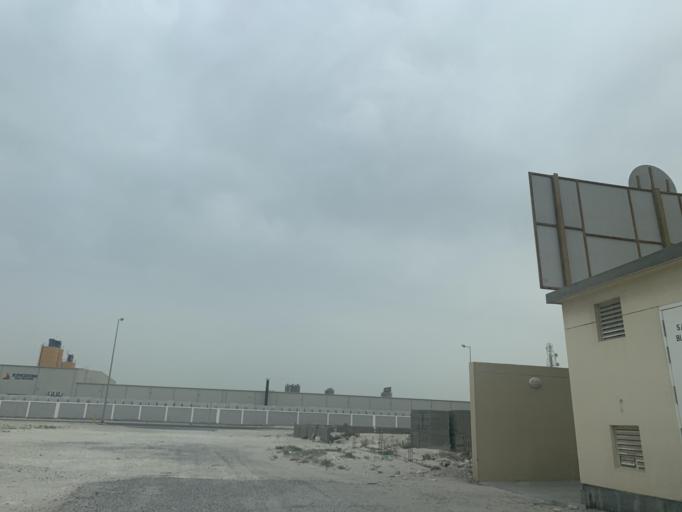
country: BH
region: Muharraq
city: Al Hadd
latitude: 26.2122
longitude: 50.6629
